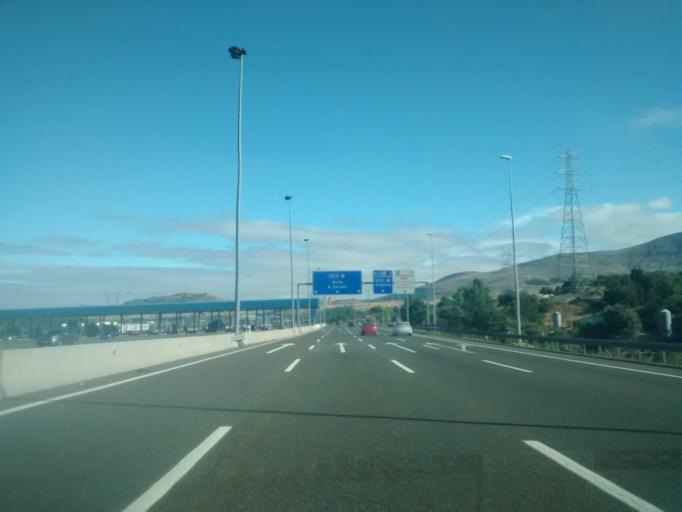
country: ES
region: Castille and Leon
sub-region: Provincia de Segovia
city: Otero de Herreros
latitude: 40.7242
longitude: -4.1918
